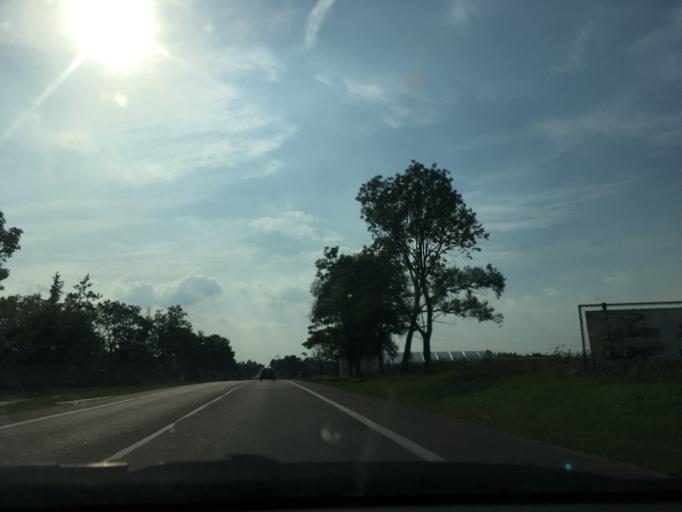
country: PL
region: Podlasie
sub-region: Powiat bialostocki
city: Suprasl
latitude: 53.1254
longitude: 23.2780
